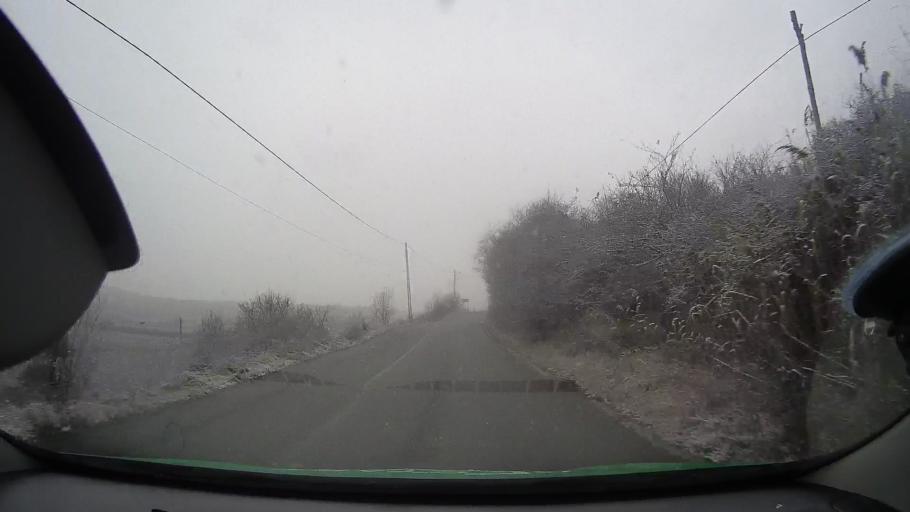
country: RO
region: Alba
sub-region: Comuna Noslac
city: Noslac
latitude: 46.3563
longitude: 23.9316
